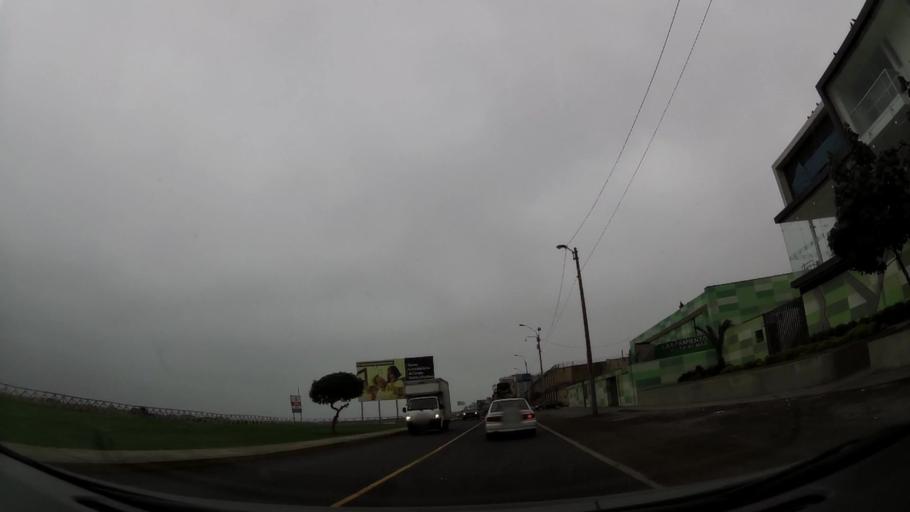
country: PE
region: Callao
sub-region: Callao
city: Callao
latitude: -12.0846
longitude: -77.0985
